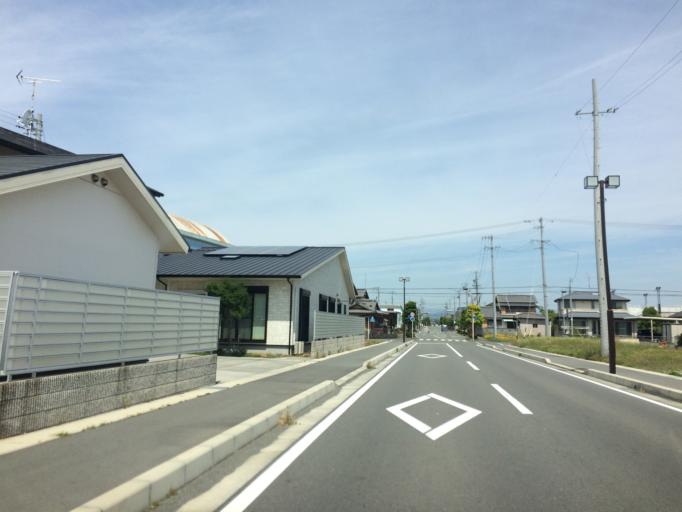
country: JP
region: Shizuoka
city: Sagara
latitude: 34.7537
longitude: 138.2548
